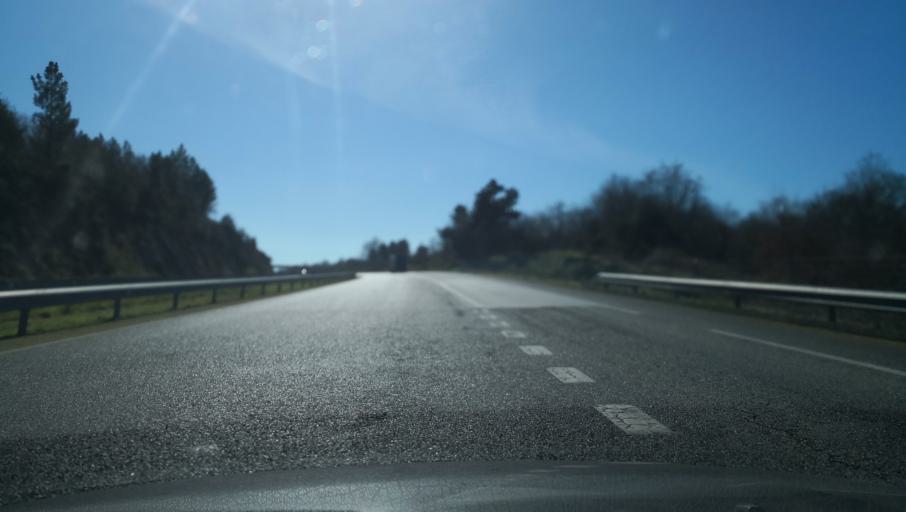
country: ES
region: Galicia
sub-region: Provincia de Ourense
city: Taboadela
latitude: 42.2712
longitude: -7.8717
